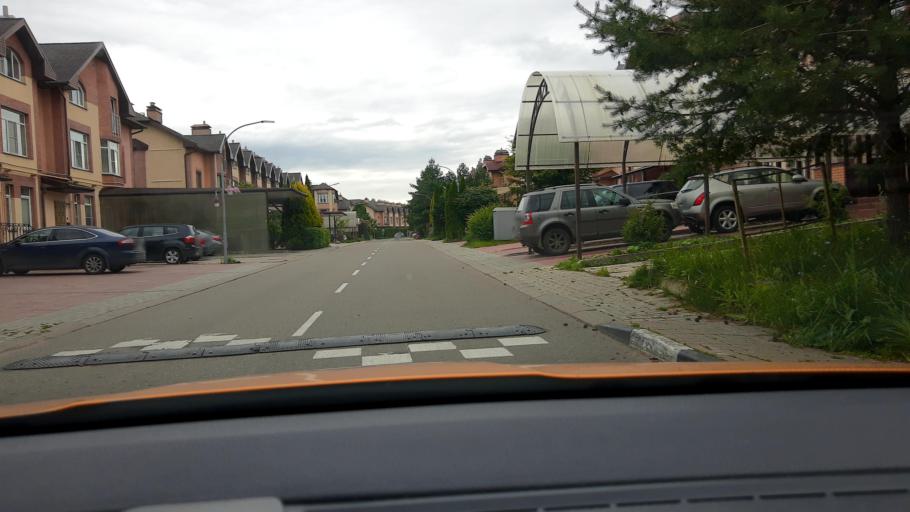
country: RU
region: Moskovskaya
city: Kommunarka
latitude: 55.5712
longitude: 37.4502
